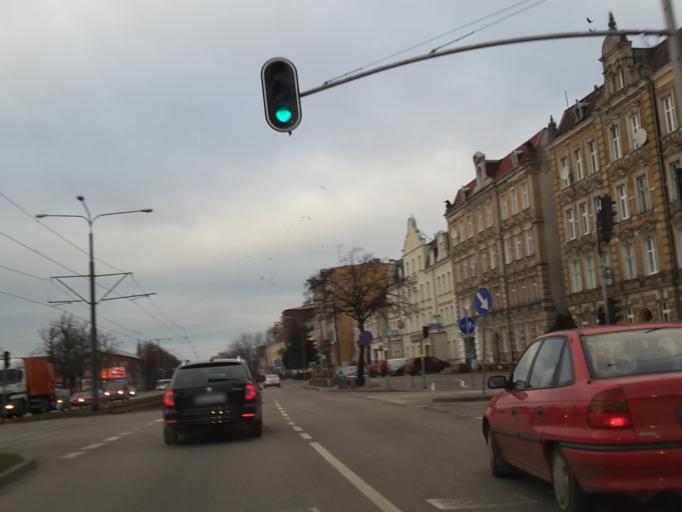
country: PL
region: Warmian-Masurian Voivodeship
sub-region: Powiat elblaski
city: Elblag
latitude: 54.1529
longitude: 19.4159
